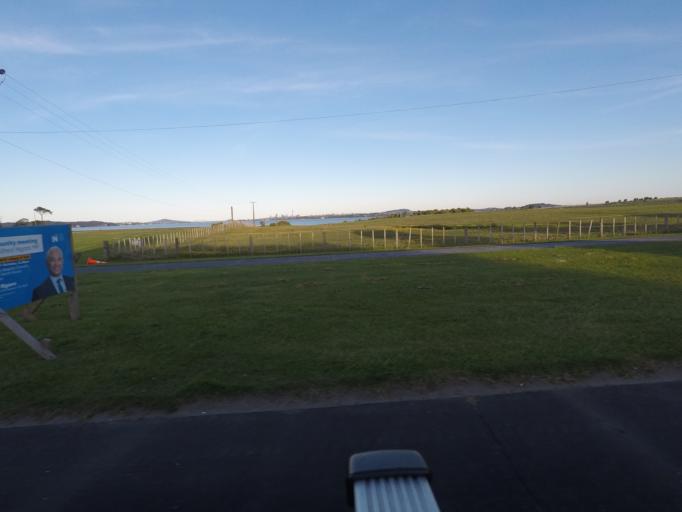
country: NZ
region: Auckland
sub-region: Auckland
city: Rosebank
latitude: -36.8518
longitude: 174.6511
